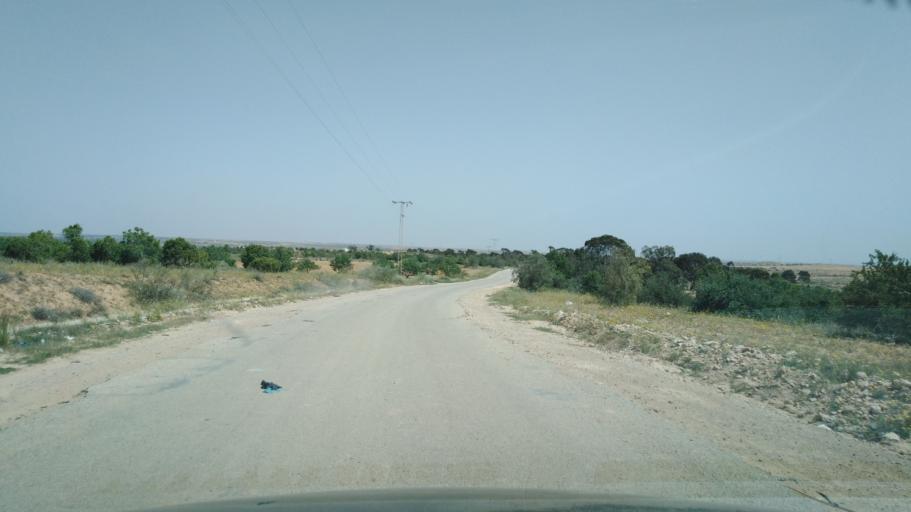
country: TN
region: Safaqis
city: Sfax
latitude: 34.7120
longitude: 10.5276
